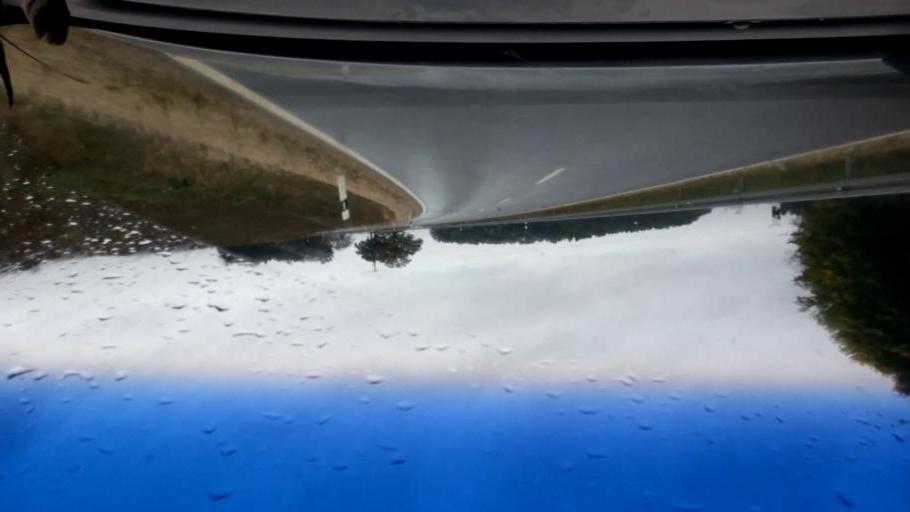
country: DE
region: Bavaria
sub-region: Upper Franconia
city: Poxdorf
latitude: 49.9282
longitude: 11.0823
